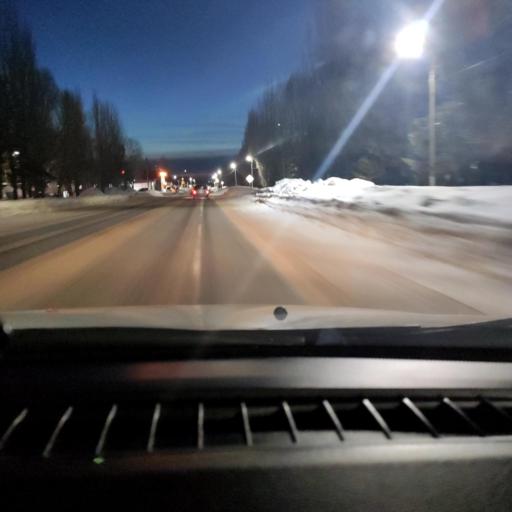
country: RU
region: Samara
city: Kinel'
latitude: 53.2679
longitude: 50.5625
